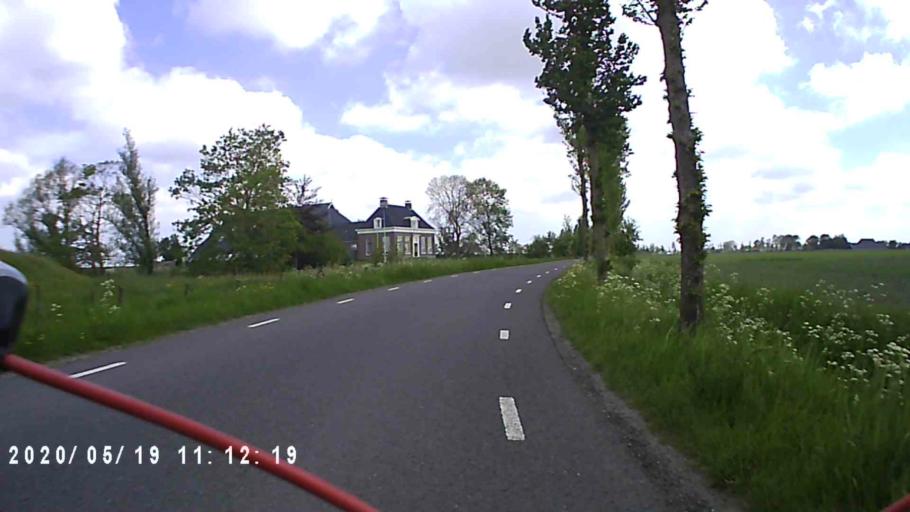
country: NL
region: Groningen
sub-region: Gemeente Zuidhorn
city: Grijpskerk
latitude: 53.2907
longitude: 6.3340
